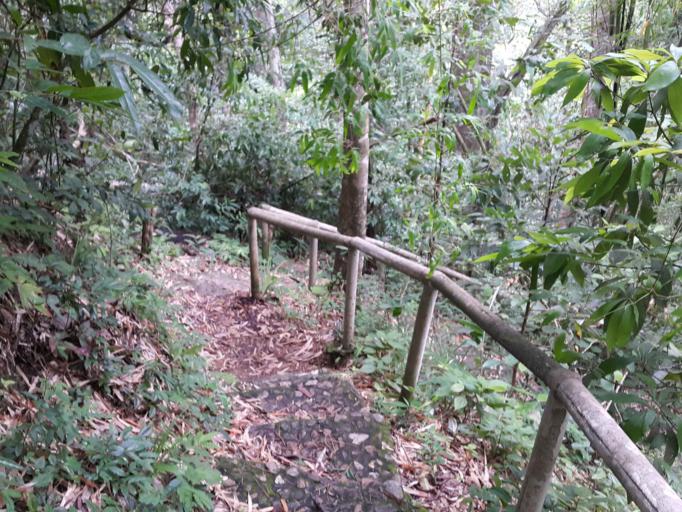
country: TH
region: Tak
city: Tak
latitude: 16.7927
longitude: 98.9217
